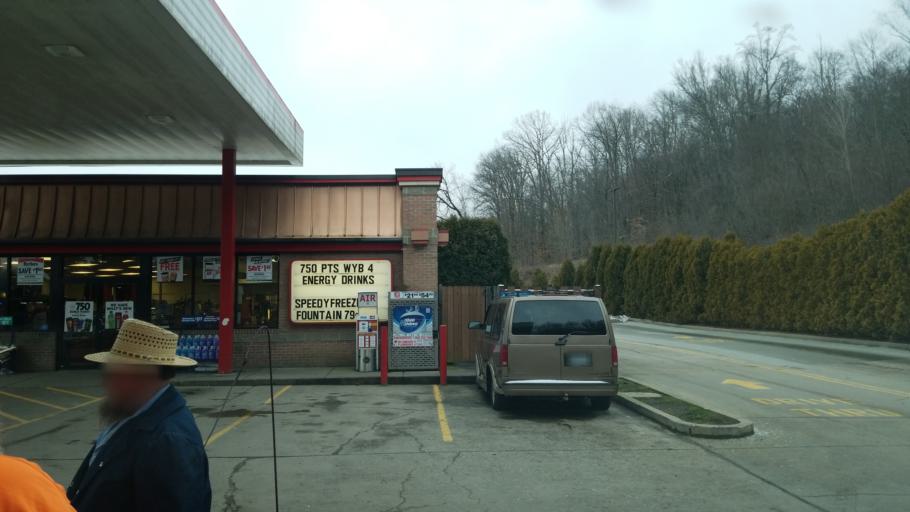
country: US
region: Ohio
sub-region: Tuscarawas County
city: Newcomerstown
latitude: 40.2865
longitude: -81.5679
